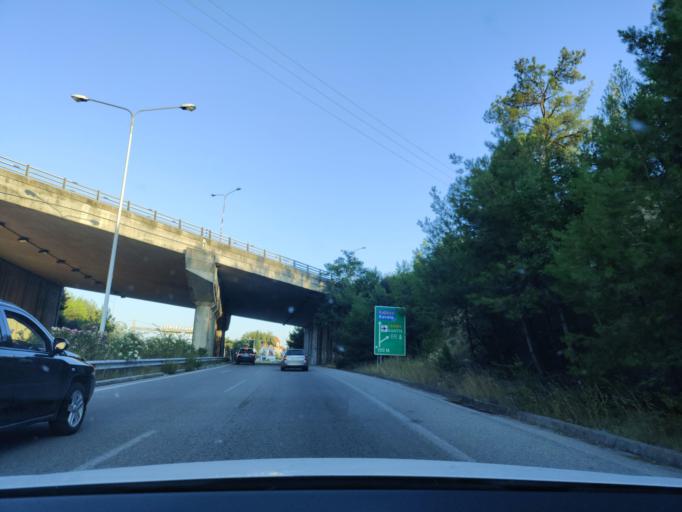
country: GR
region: East Macedonia and Thrace
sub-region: Nomos Kavalas
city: Amygdaleonas
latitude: 40.9430
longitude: 24.3745
